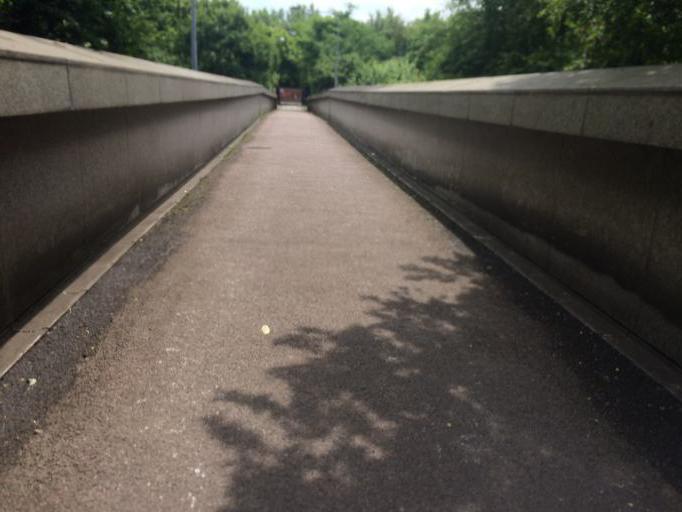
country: GB
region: England
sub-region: Milton Keynes
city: Milton Keynes
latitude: 52.0428
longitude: -0.7682
